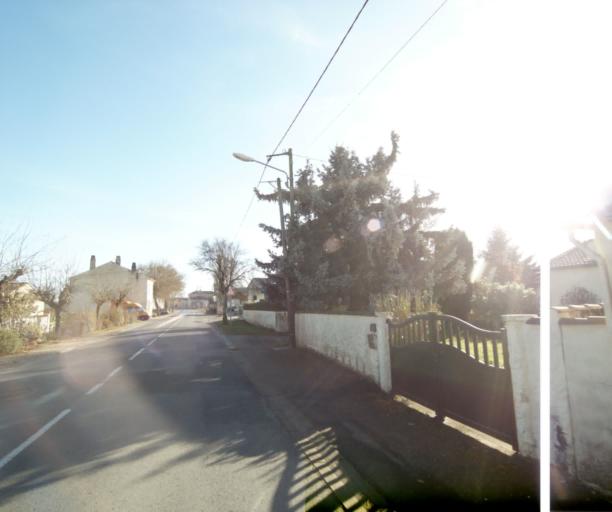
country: FR
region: Poitou-Charentes
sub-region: Departement de la Charente-Maritime
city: Burie
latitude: 45.7787
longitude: -0.4227
